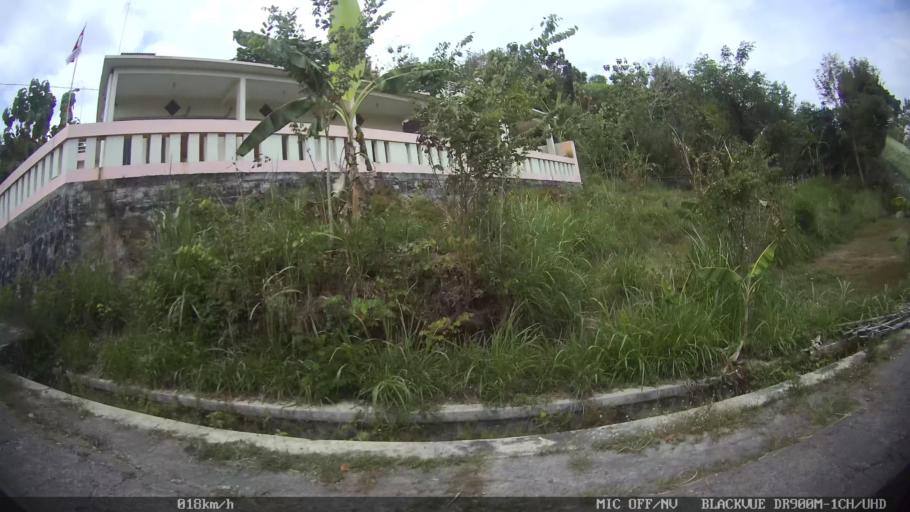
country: ID
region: Central Java
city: Candi Prambanan
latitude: -7.7834
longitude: 110.5017
